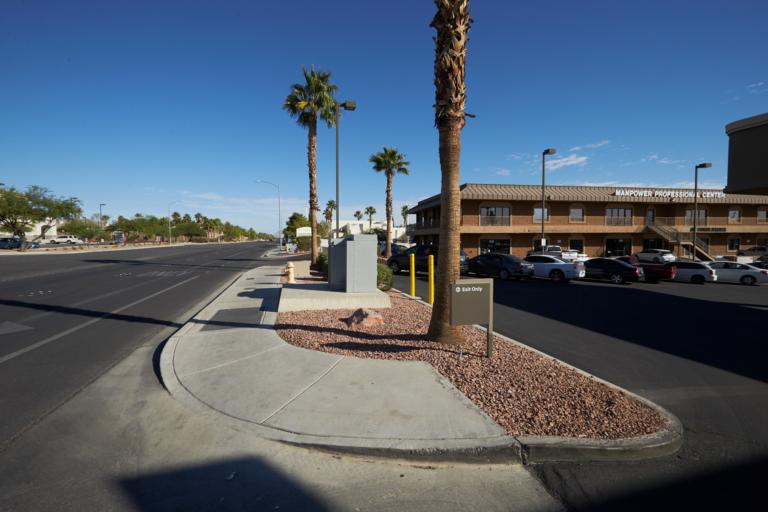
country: US
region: Nevada
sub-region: Clark County
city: Spring Valley
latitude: 36.1445
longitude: -115.2699
